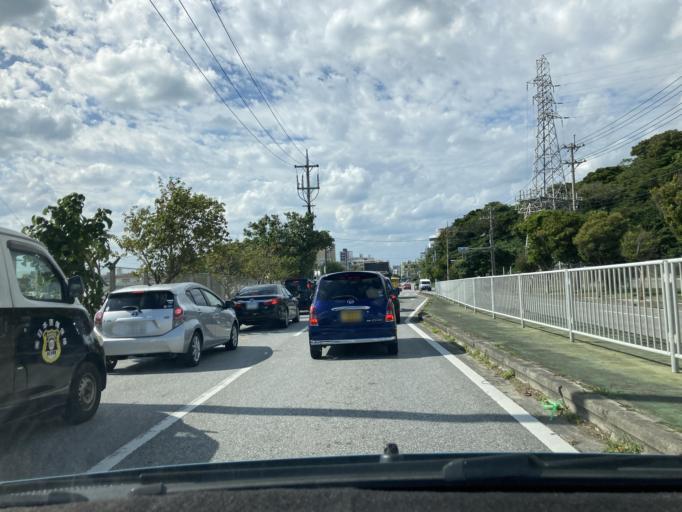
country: JP
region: Okinawa
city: Chatan
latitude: 26.3079
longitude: 127.7671
